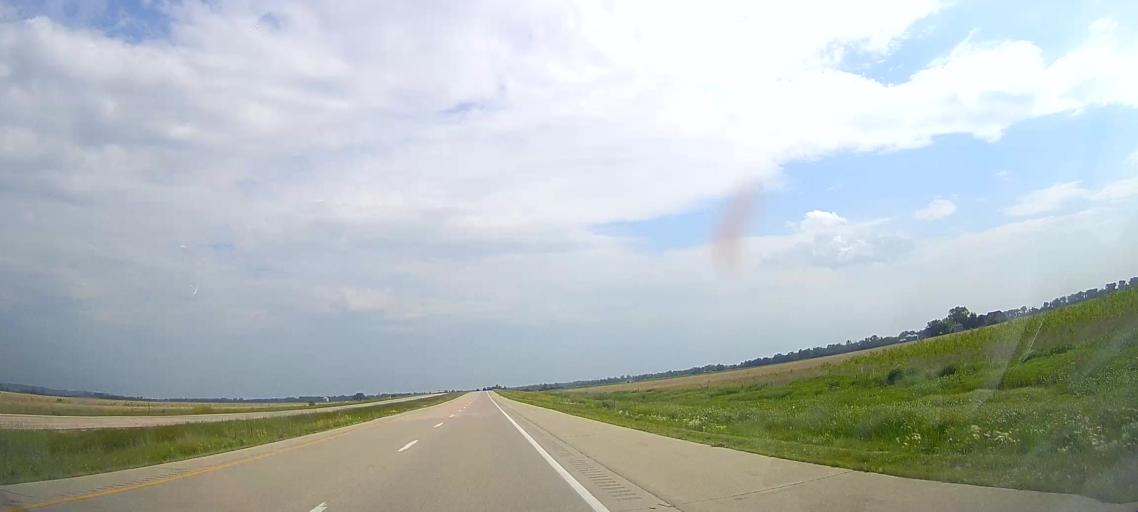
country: US
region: Nebraska
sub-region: Burt County
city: Tekamah
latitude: 41.8698
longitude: -96.1037
